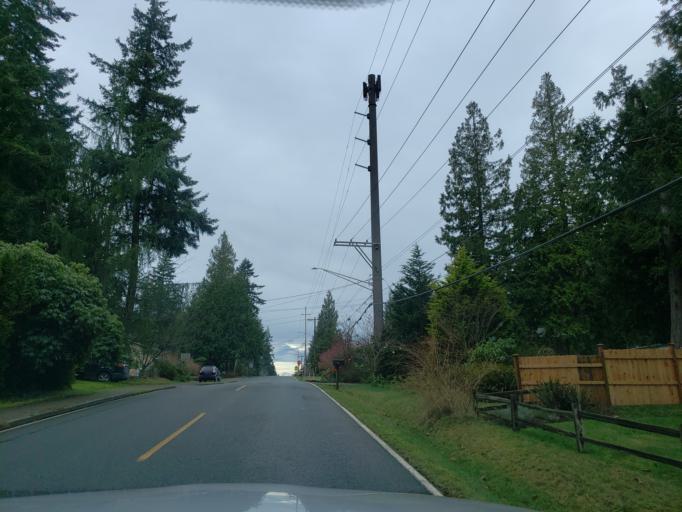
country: US
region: Washington
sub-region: Snohomish County
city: Meadowdale
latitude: 47.8287
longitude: -122.3452
